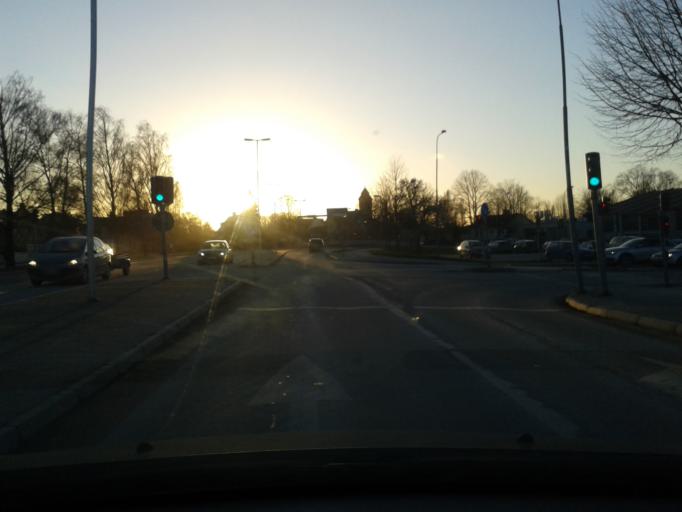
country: SE
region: Gotland
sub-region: Gotland
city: Visby
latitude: 57.6360
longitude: 18.3024
